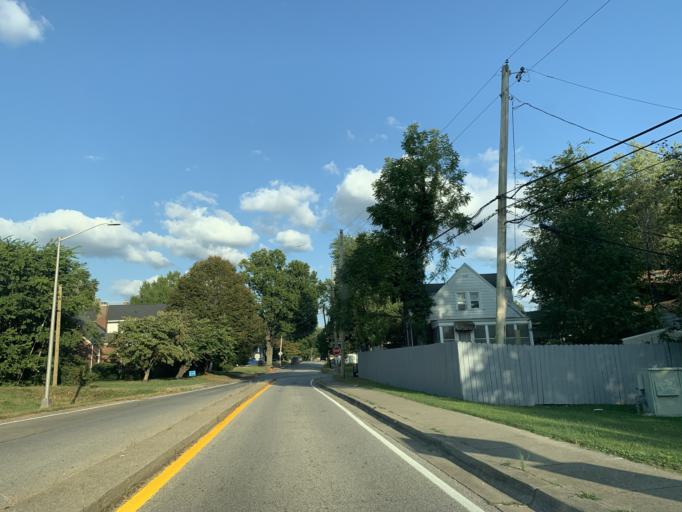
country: US
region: Kentucky
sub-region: Jefferson County
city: Audubon Park
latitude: 38.1892
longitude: -85.7634
